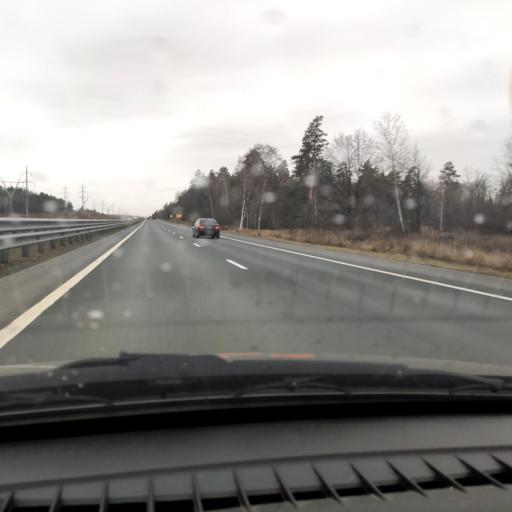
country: RU
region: Samara
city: Povolzhskiy
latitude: 53.5164
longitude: 49.7247
